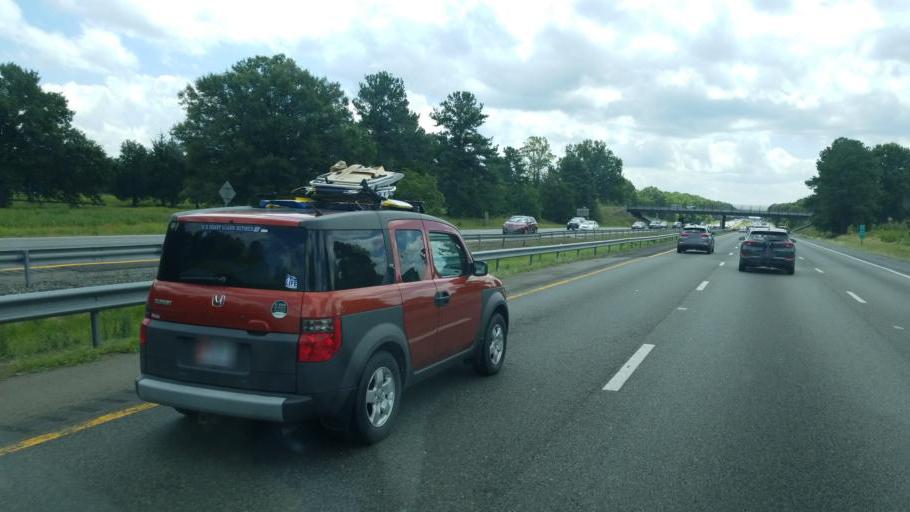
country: US
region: Virginia
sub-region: Hanover County
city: Ashland
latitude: 37.7621
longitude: -77.4604
